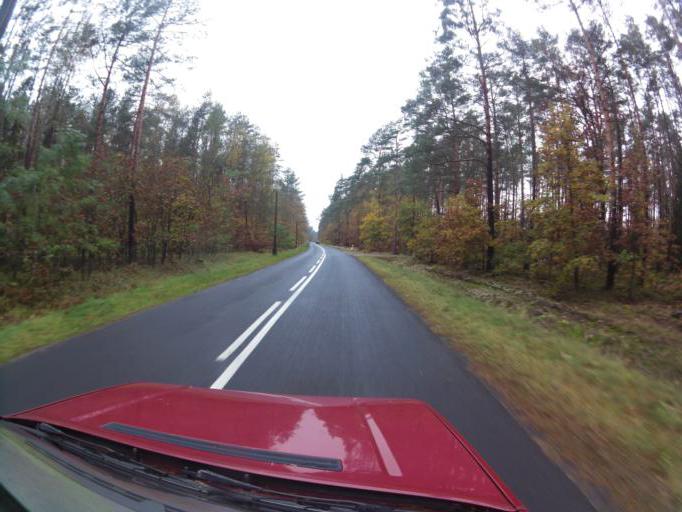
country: PL
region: West Pomeranian Voivodeship
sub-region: Powiat policki
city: Dobra
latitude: 53.5981
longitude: 14.3436
